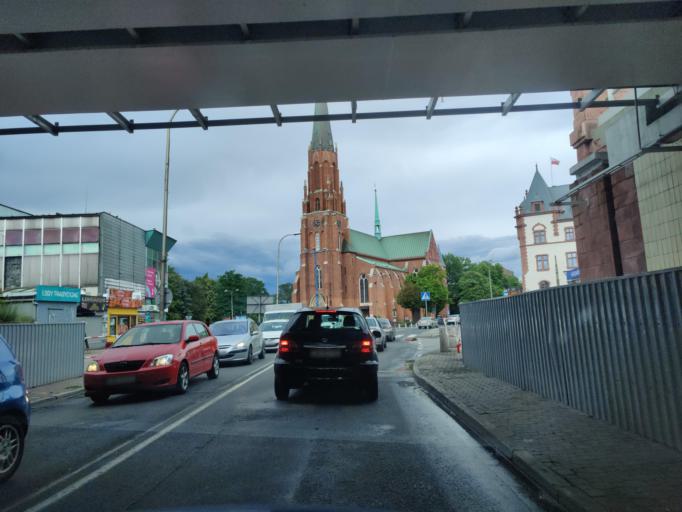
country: PL
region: Silesian Voivodeship
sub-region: Myslowice
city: Myslowice
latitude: 50.2419
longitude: 19.1376
